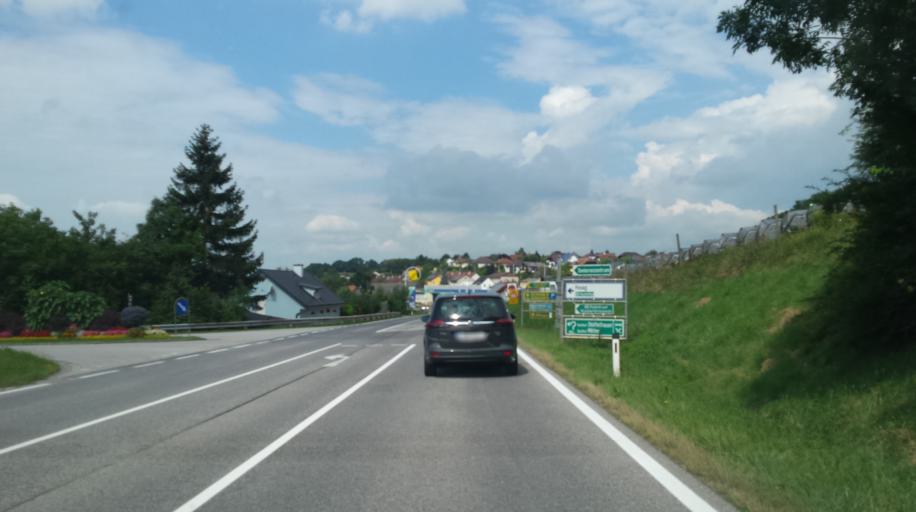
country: AT
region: Lower Austria
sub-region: Politischer Bezirk Amstetten
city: Haag
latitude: 48.1147
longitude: 14.5743
